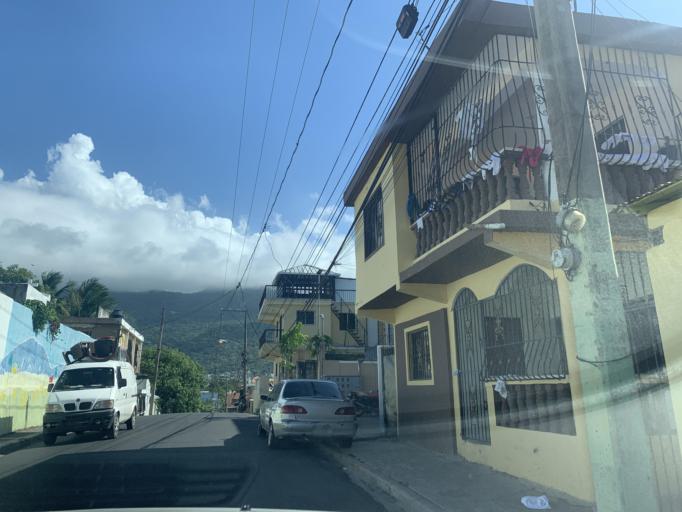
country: DO
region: Puerto Plata
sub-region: Puerto Plata
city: Puerto Plata
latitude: 19.7942
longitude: -70.6941
